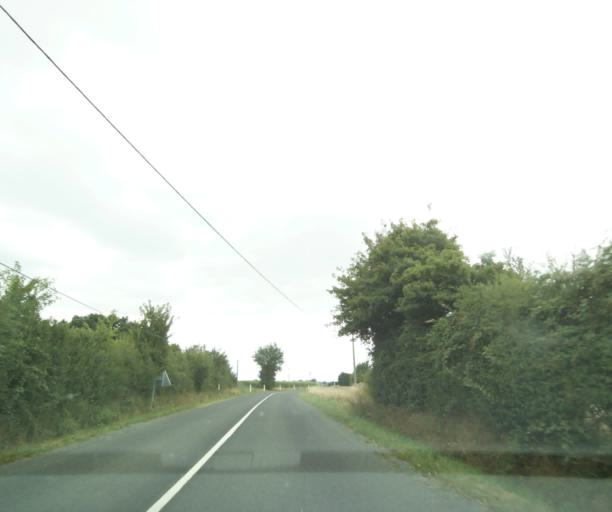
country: FR
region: Pays de la Loire
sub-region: Departement de la Sarthe
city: Precigne
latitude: 47.7626
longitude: -0.3160
